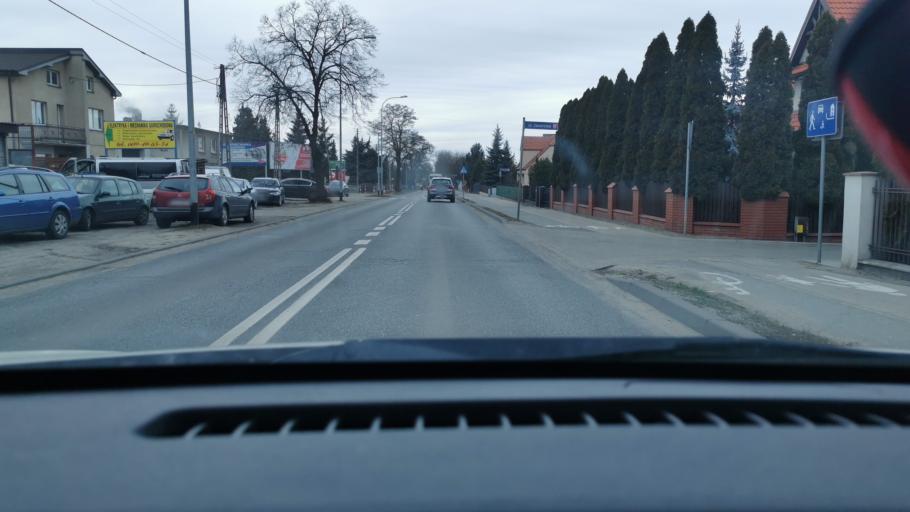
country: PL
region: Greater Poland Voivodeship
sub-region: Powiat ostrowski
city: Ostrow Wielkopolski
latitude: 51.6431
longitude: 17.8655
